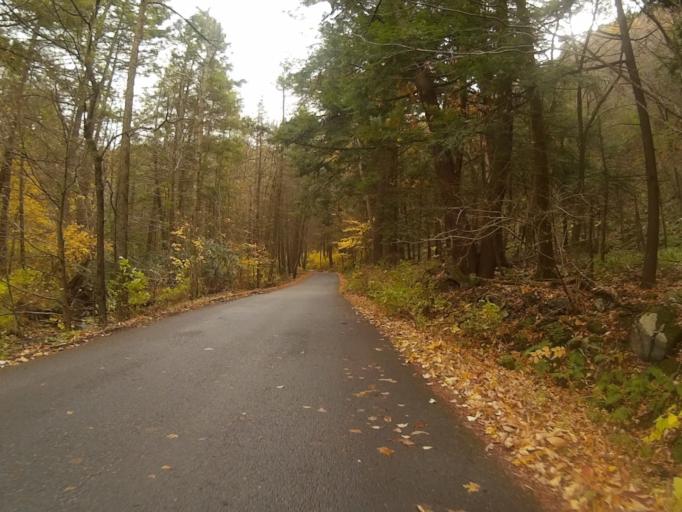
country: US
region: Pennsylvania
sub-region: Centre County
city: Boalsburg
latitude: 40.7638
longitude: -77.7558
